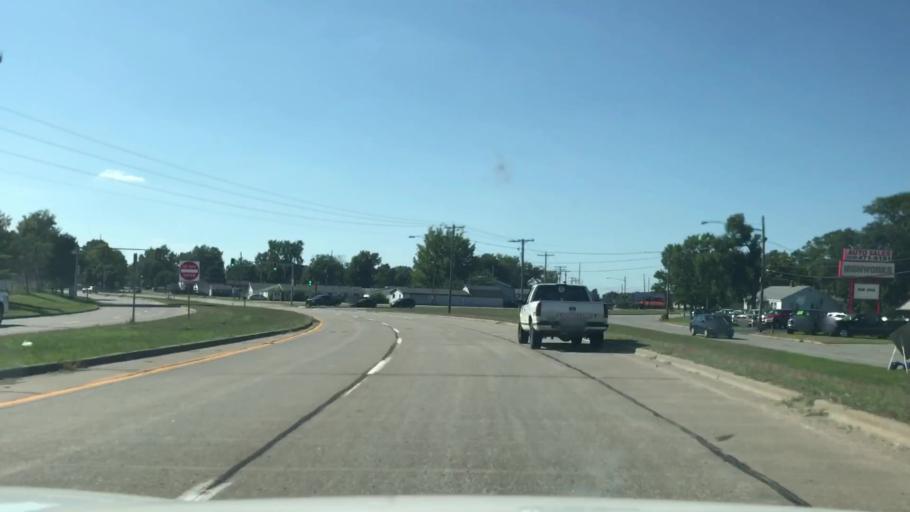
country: US
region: Illinois
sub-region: Madison County
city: Roxana
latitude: 38.8607
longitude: -90.0732
